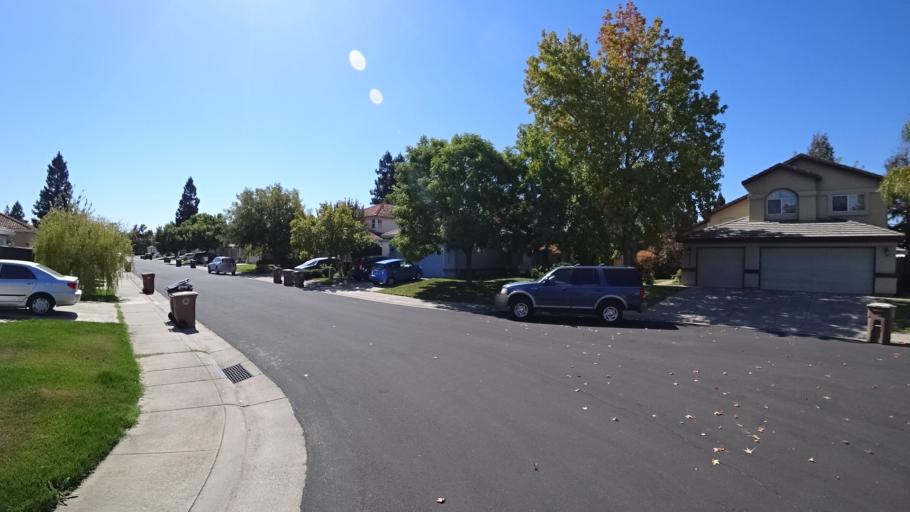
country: US
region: California
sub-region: Sacramento County
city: Laguna
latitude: 38.4360
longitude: -121.4294
